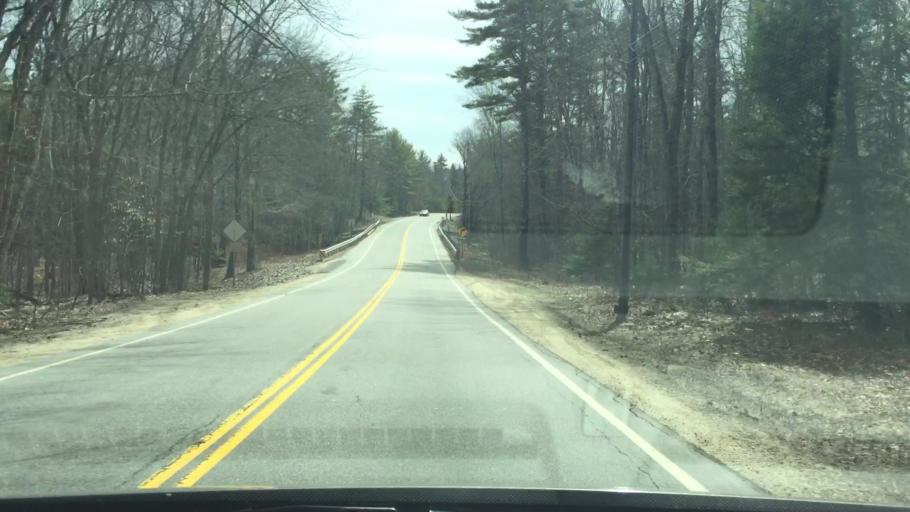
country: US
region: New Hampshire
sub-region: Strafford County
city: Barrington
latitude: 43.2413
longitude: -71.0550
